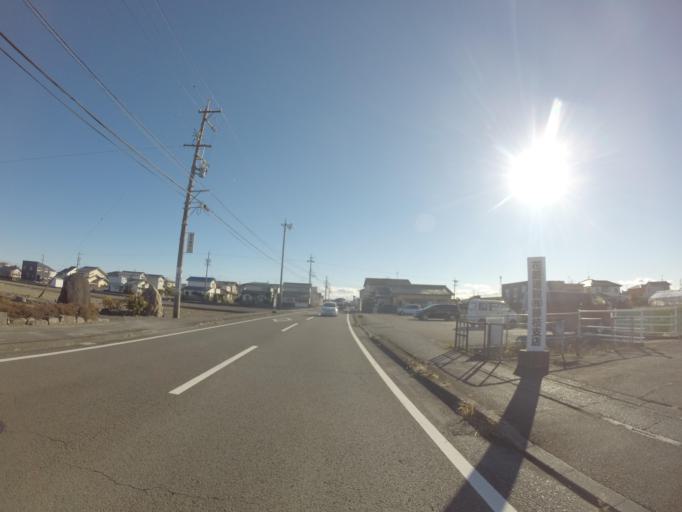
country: JP
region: Shizuoka
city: Fujieda
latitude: 34.8339
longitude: 138.2576
